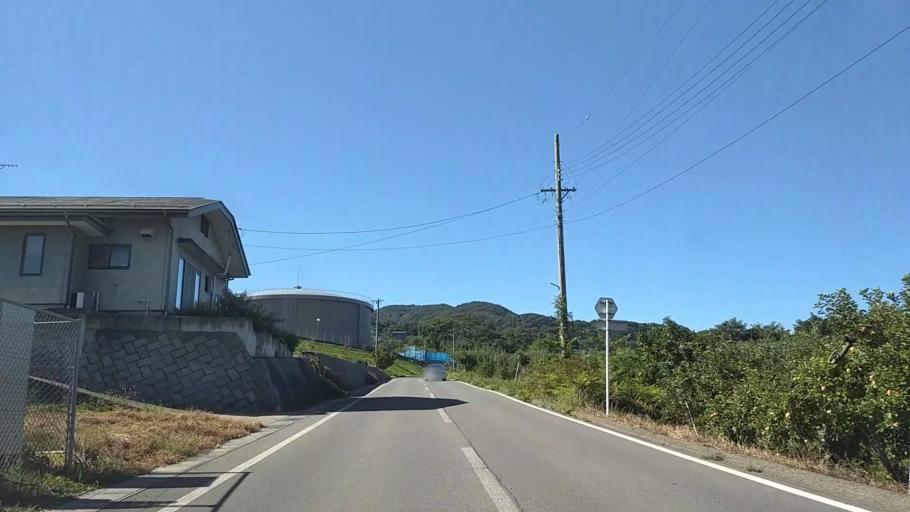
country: JP
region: Nagano
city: Nagano-shi
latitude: 36.5808
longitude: 138.1256
